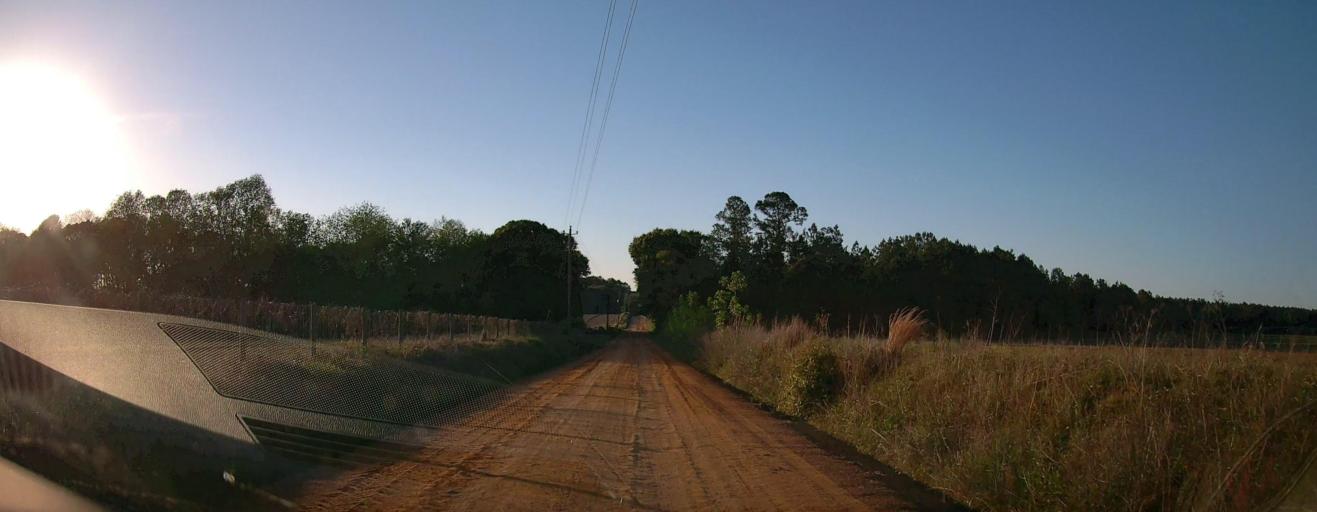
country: US
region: Georgia
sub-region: Irwin County
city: Ocilla
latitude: 31.6440
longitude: -83.2216
